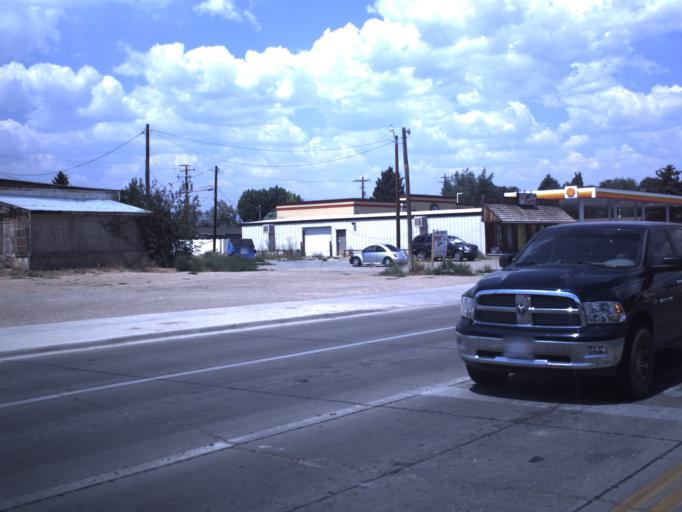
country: US
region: Utah
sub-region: Uintah County
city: Vernal
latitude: 40.4558
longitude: -109.5380
